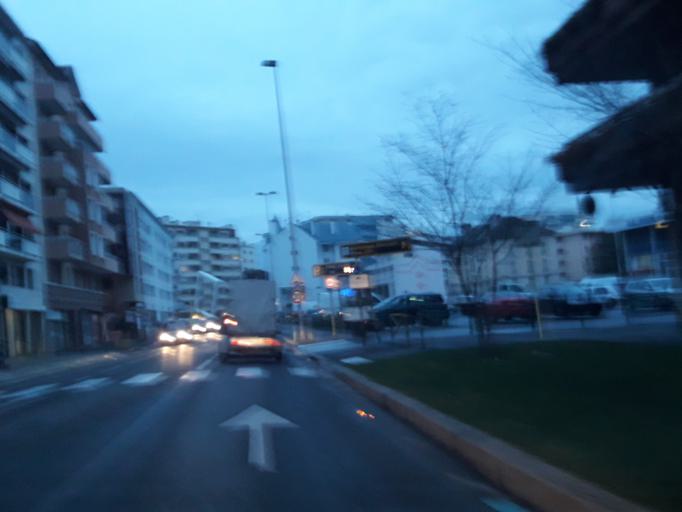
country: FR
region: Rhone-Alpes
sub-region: Departement de la Haute-Savoie
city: Annemasse
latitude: 46.1924
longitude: 6.2322
